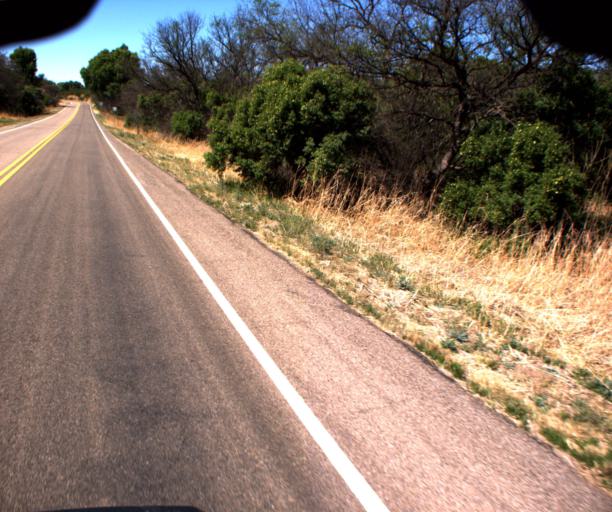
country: US
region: Arizona
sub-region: Santa Cruz County
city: Rio Rico
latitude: 31.5359
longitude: -110.7611
